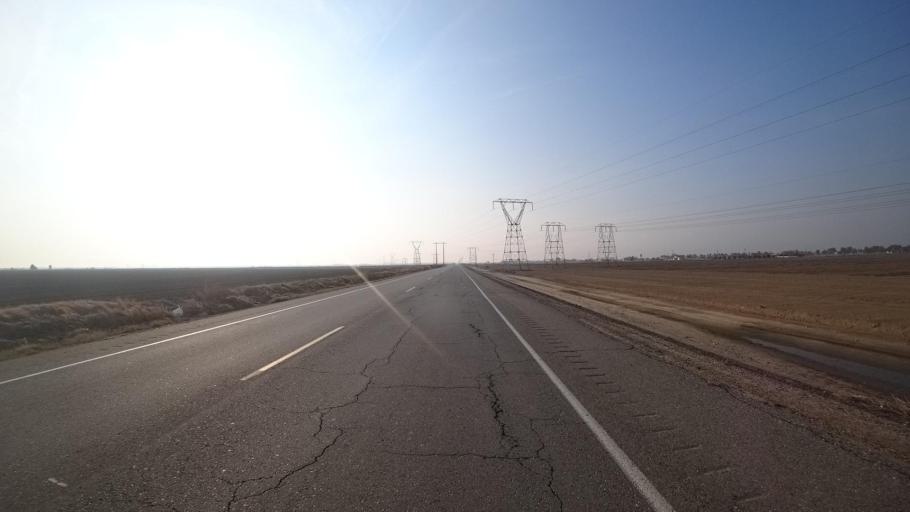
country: US
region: California
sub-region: Kern County
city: Weedpatch
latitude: 35.1828
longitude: -118.9146
